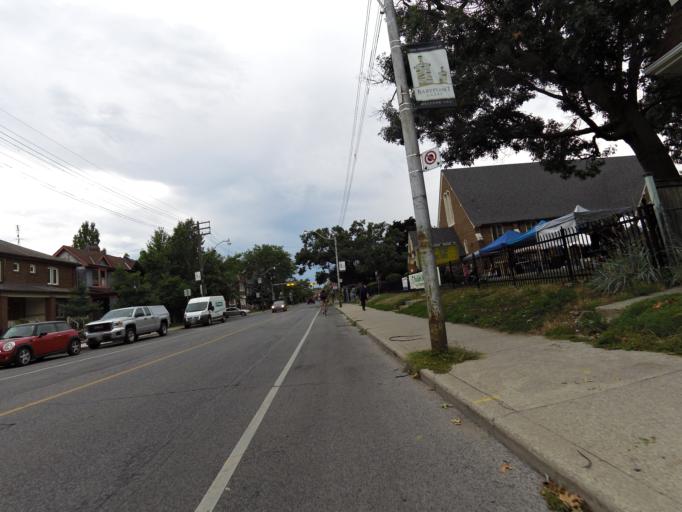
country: CA
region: Ontario
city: Toronto
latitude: 43.6591
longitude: -79.4843
